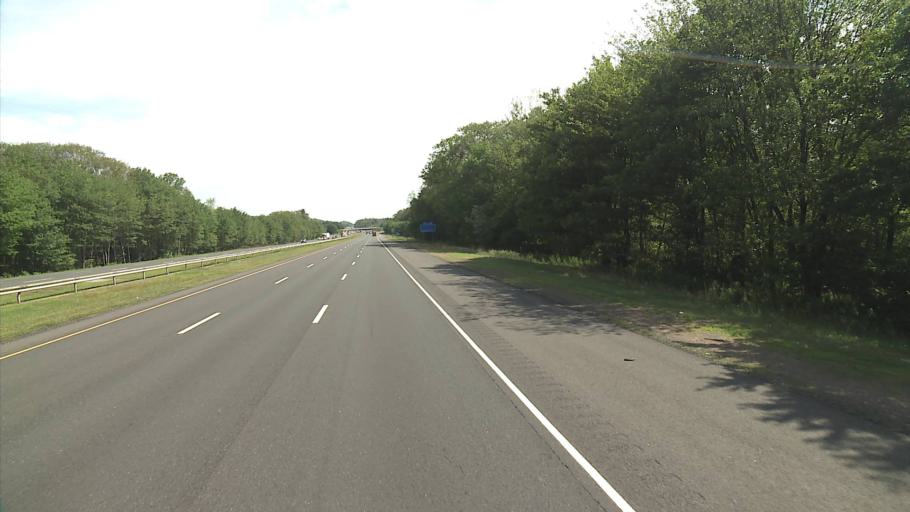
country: US
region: Massachusetts
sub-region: Hampden County
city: Holland
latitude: 41.9699
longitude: -72.1870
